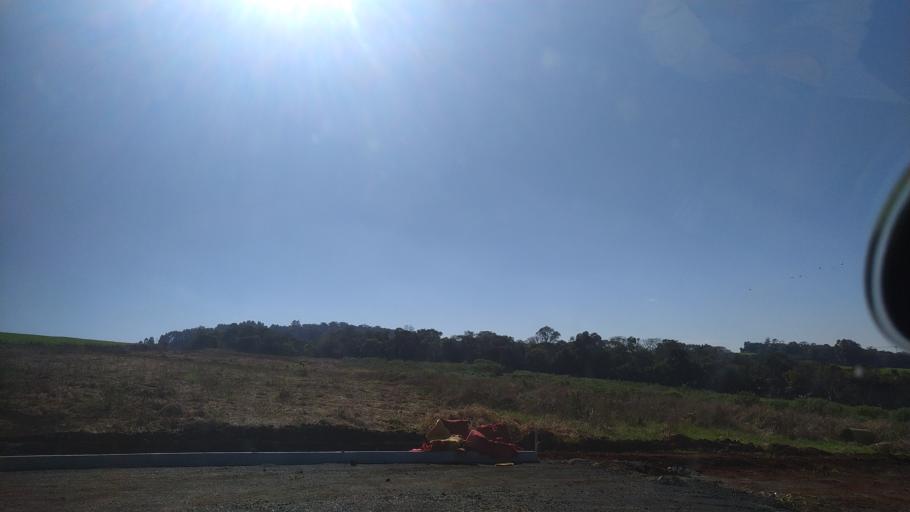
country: BR
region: Santa Catarina
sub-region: Chapeco
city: Chapeco
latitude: -27.0856
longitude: -52.6905
